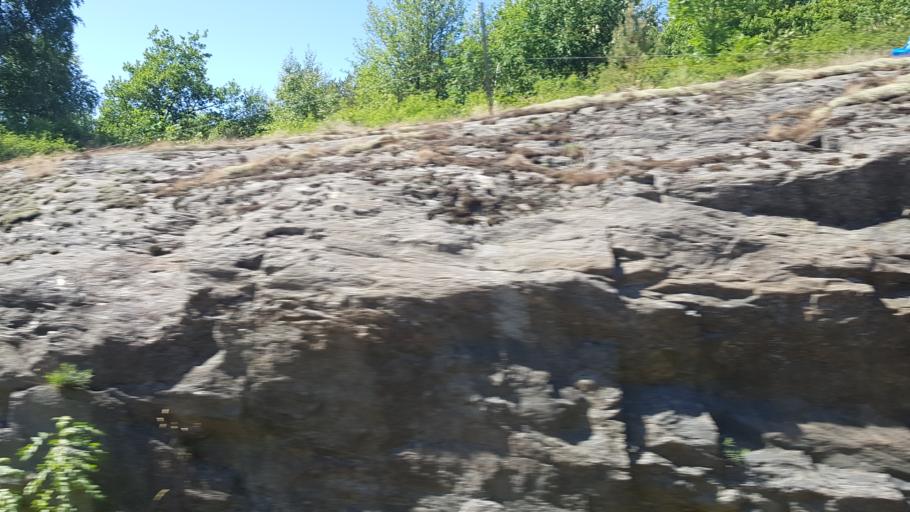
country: SE
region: Vaestra Goetaland
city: Ronnang
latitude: 57.9929
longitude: 11.6602
